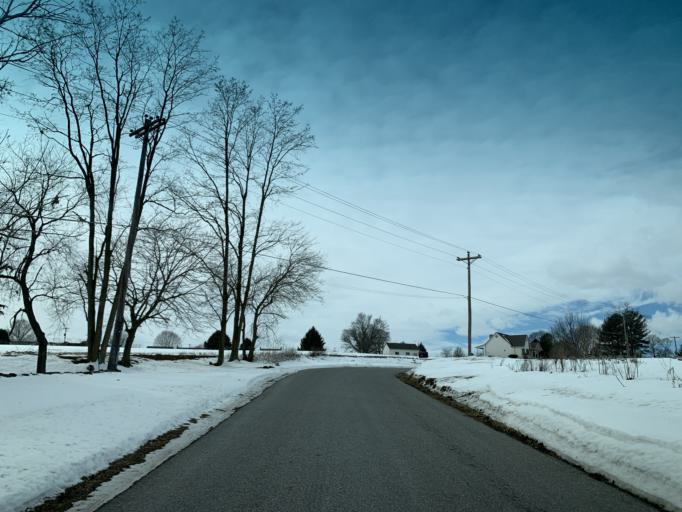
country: US
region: Pennsylvania
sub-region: York County
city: Red Lion
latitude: 39.8343
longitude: -76.6148
